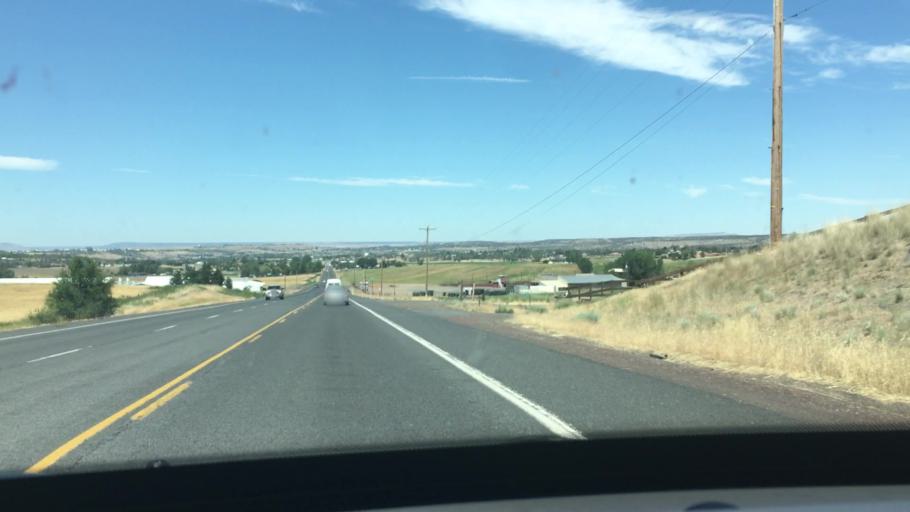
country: US
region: Oregon
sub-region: Jefferson County
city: Madras
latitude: 44.5833
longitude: -121.1540
